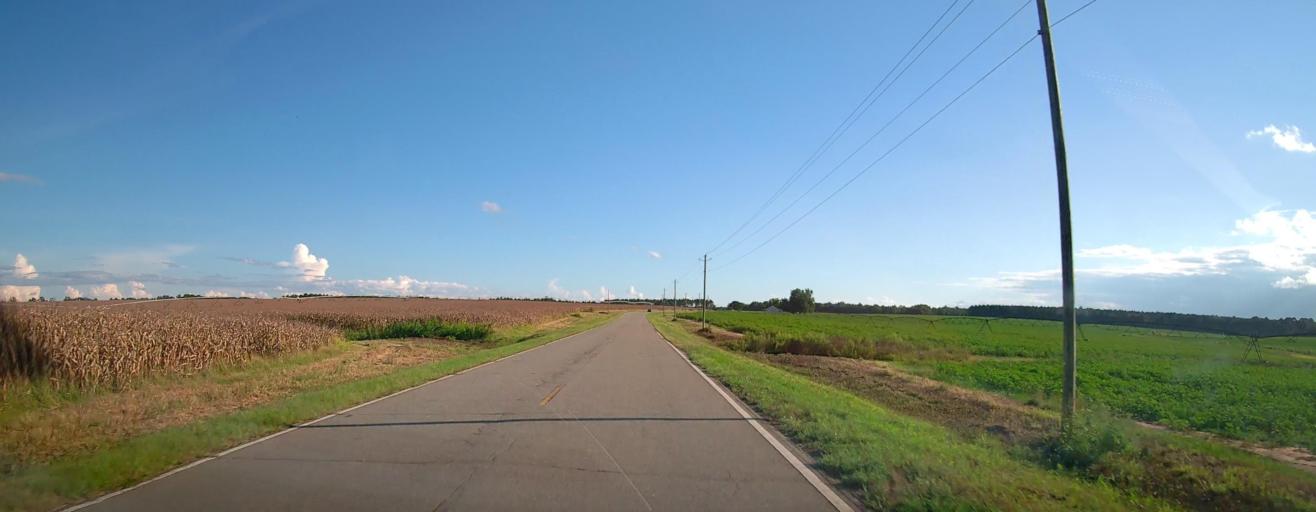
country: US
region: Georgia
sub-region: Pulaski County
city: Hawkinsville
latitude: 32.3824
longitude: -83.4587
